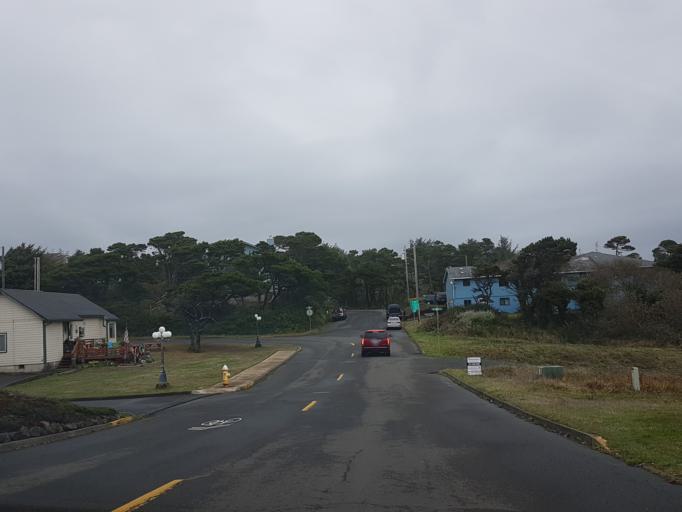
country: US
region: Oregon
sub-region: Lincoln County
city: Newport
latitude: 44.6420
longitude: -124.0605
